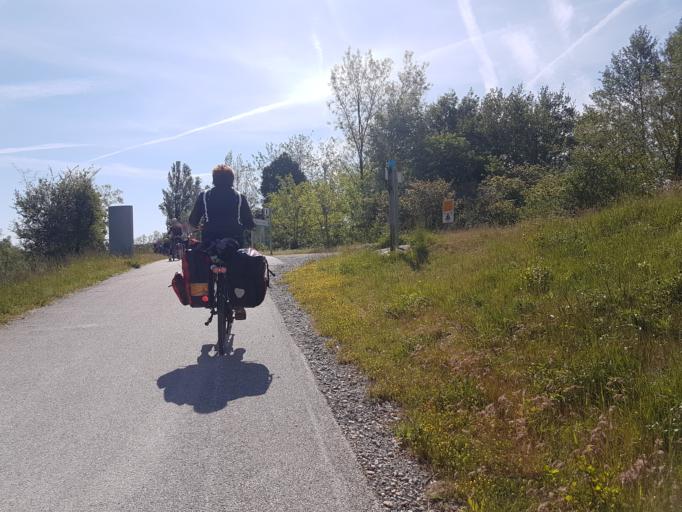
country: FR
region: Rhone-Alpes
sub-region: Departement de l'Ardeche
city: La Voulte-sur-Rhone
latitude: 44.7727
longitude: 4.7678
